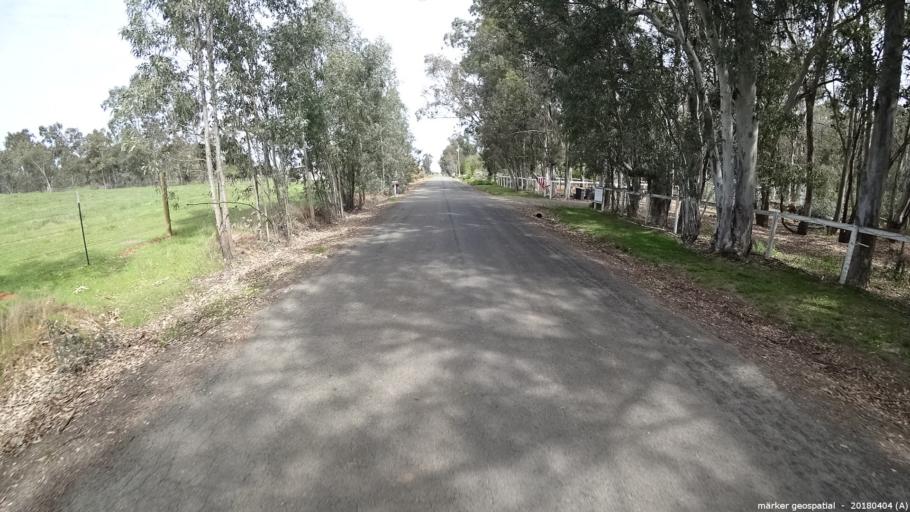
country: US
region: California
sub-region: Sacramento County
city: Clay
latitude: 38.3237
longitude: -121.1499
